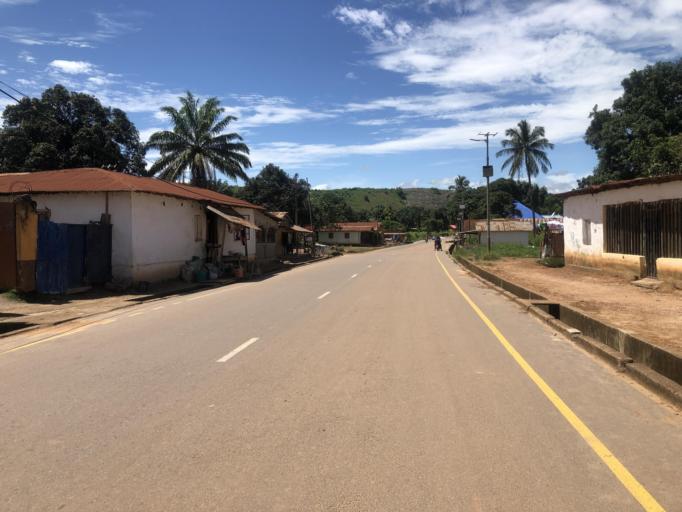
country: SL
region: Eastern Province
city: Koidu
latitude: 8.6413
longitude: -10.9666
